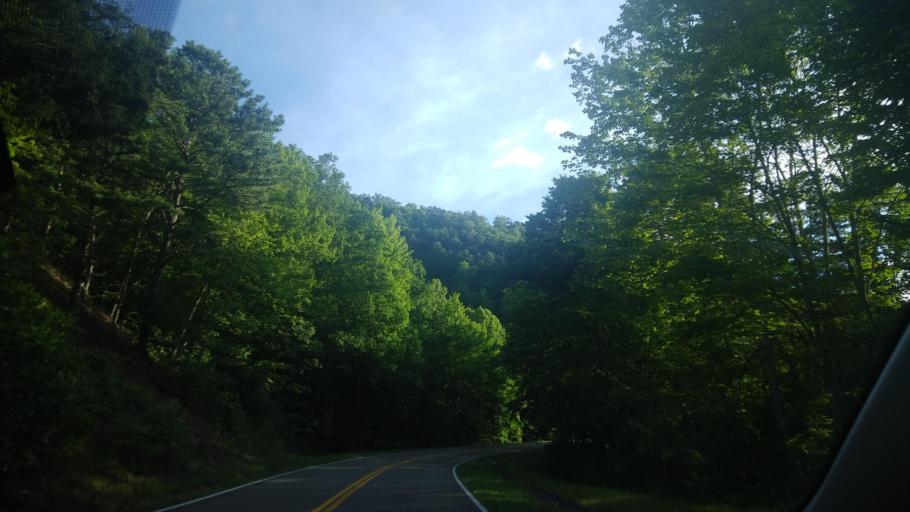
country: US
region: Tennessee
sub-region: Cocke County
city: Newport
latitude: 35.8085
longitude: -83.2315
